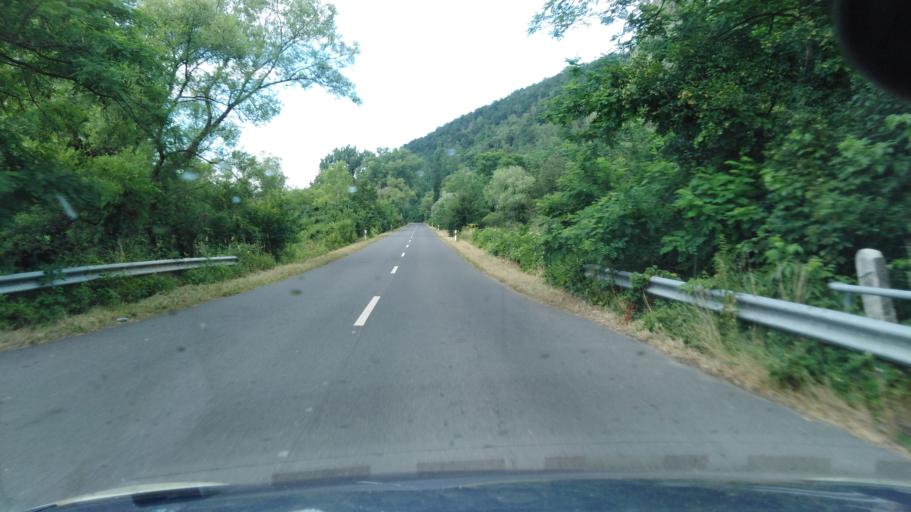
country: HU
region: Nograd
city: Szecseny
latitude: 48.1935
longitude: 19.5300
